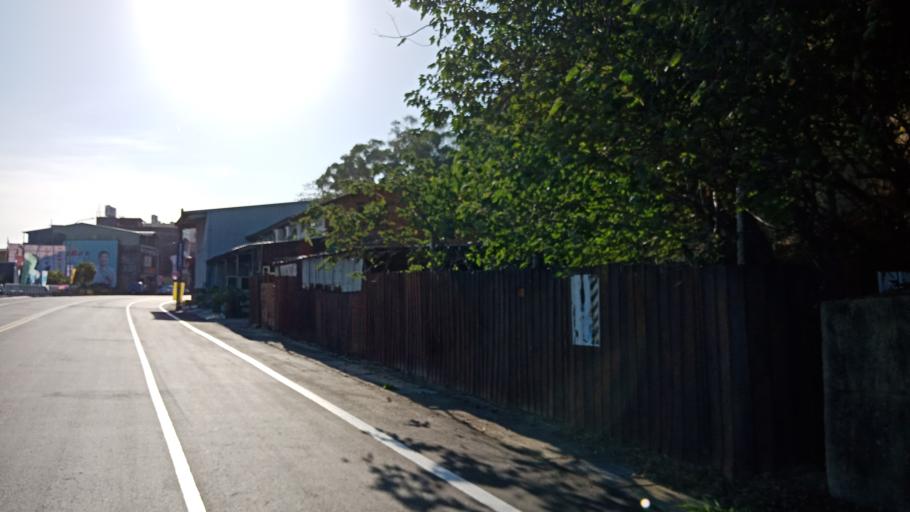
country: TW
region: Taiwan
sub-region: Miaoli
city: Miaoli
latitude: 24.4919
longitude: 120.6856
